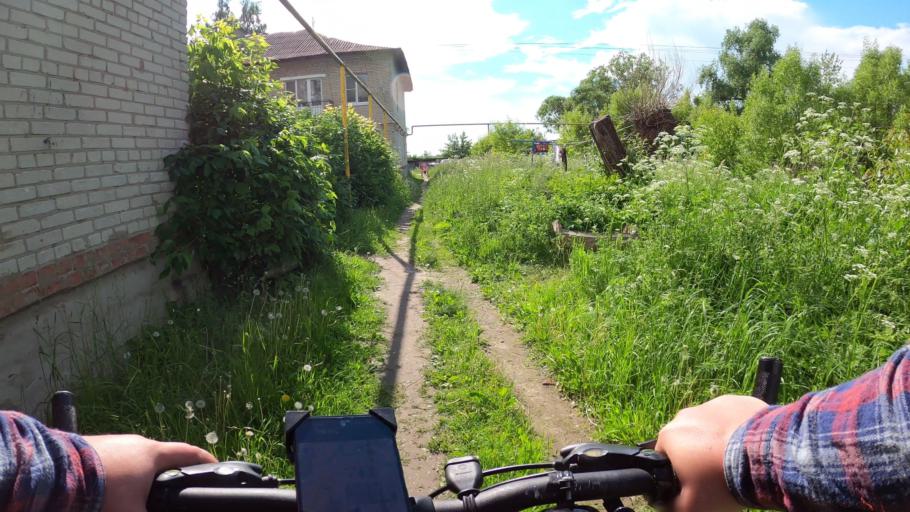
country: RU
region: Moskovskaya
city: Konobeyevo
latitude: 55.4143
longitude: 38.6566
